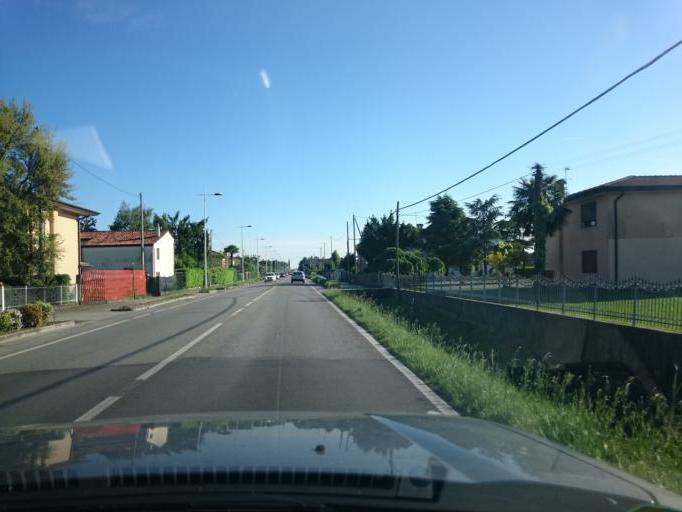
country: IT
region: Veneto
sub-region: Provincia di Venezia
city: Pianiga
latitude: 45.4683
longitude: 11.9975
